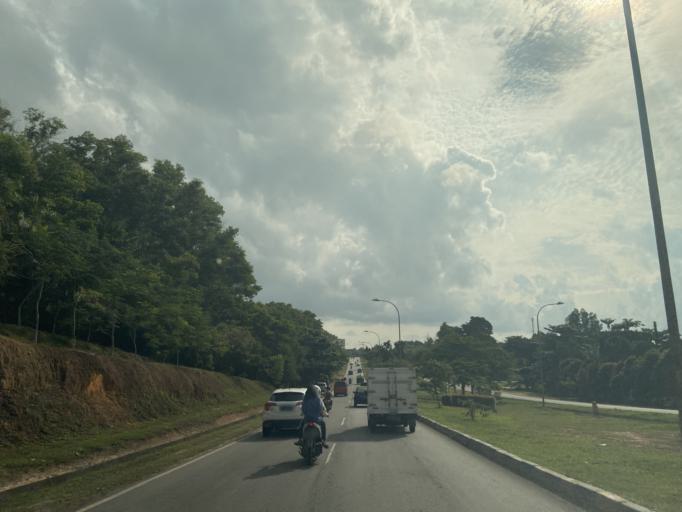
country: SG
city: Singapore
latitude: 1.0995
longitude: 104.0712
